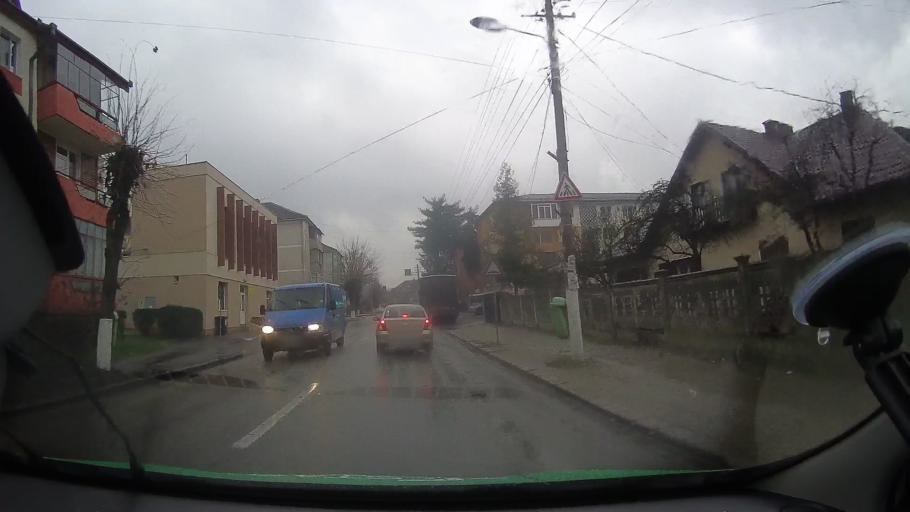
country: RO
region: Hunedoara
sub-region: Municipiul Brad
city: Brad
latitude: 46.1257
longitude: 22.7911
